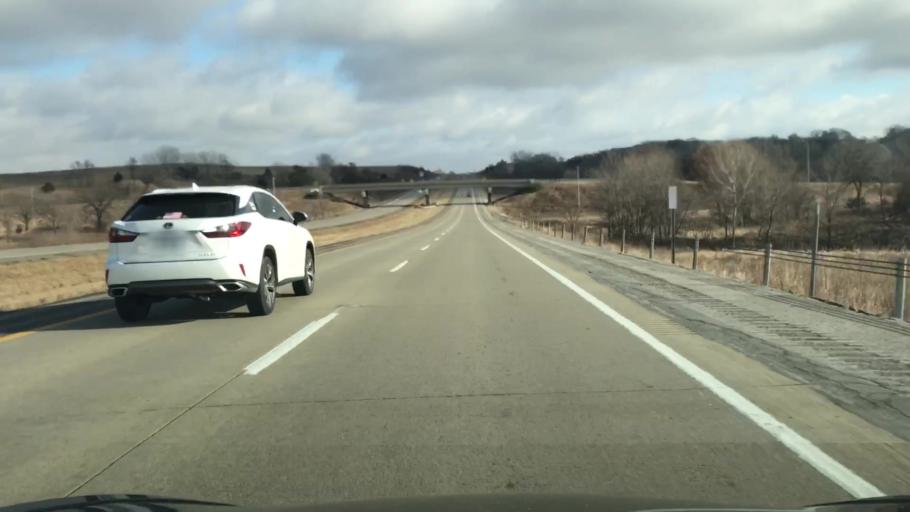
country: US
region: Iowa
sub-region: Cass County
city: Atlantic
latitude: 41.4969
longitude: -94.7613
